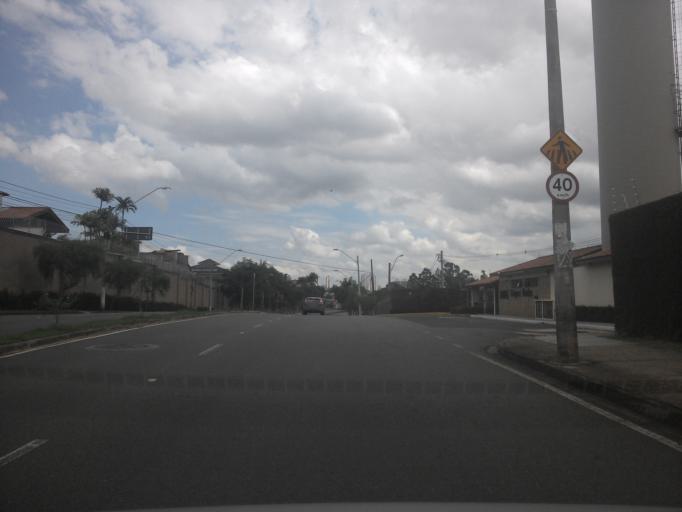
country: BR
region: Sao Paulo
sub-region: Campinas
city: Campinas
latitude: -22.8664
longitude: -47.0298
